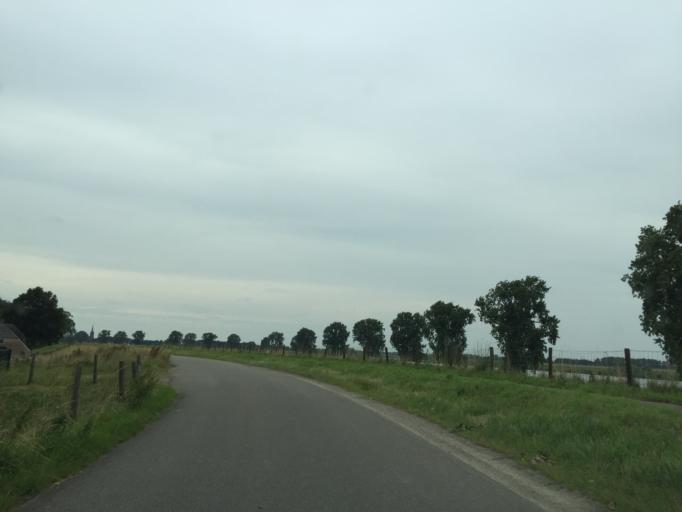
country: NL
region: Gelderland
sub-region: Gemeente Wijchen
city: Bergharen
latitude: 51.8103
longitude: 5.6458
